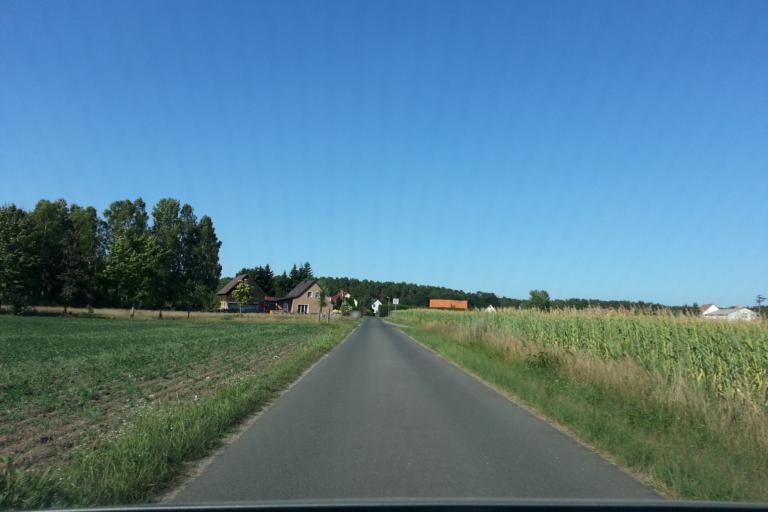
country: DE
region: Mecklenburg-Vorpommern
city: Eggesin
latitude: 53.6816
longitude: 14.0379
